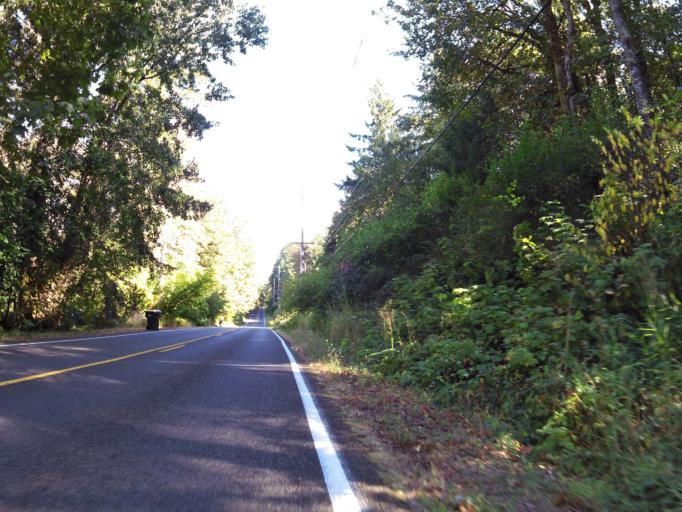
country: US
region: Washington
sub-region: Thurston County
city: Olympia
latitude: 47.0575
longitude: -123.0117
